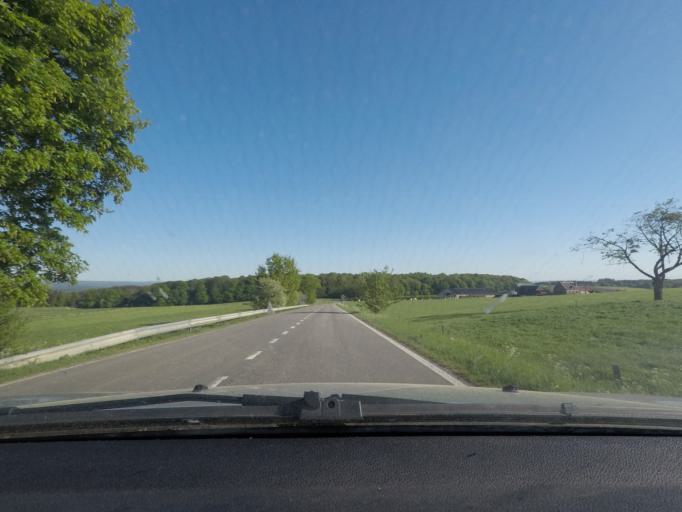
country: BE
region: Wallonia
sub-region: Province de Namur
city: Rochefort
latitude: 50.2159
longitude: 5.1473
